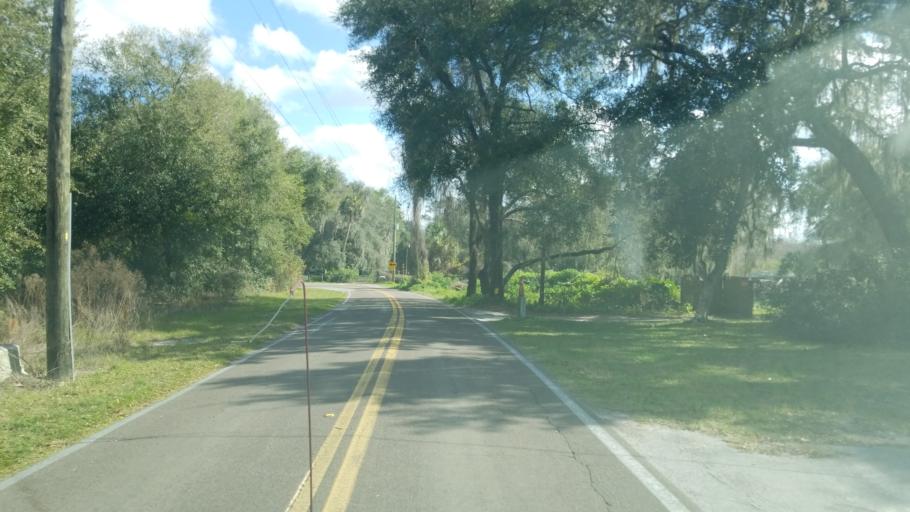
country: US
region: Florida
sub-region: Citrus County
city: Floral City
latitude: 28.7511
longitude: -82.2543
